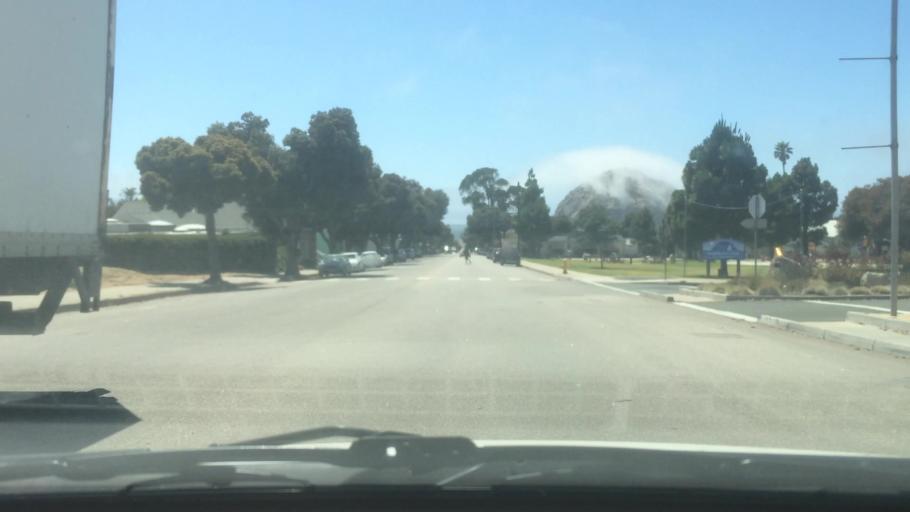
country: US
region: California
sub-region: San Luis Obispo County
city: Morro Bay
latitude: 35.3660
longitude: -120.8435
